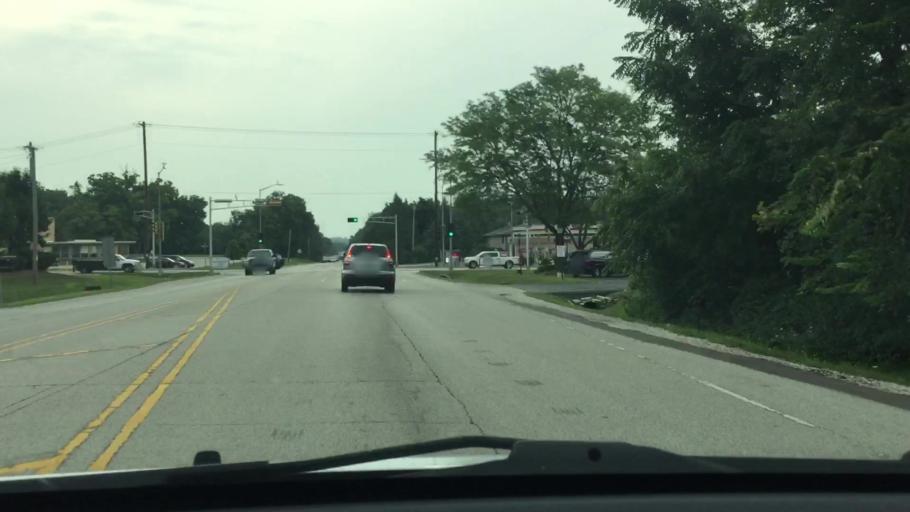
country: US
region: Wisconsin
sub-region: Waukesha County
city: New Berlin
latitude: 42.9955
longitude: -88.0896
